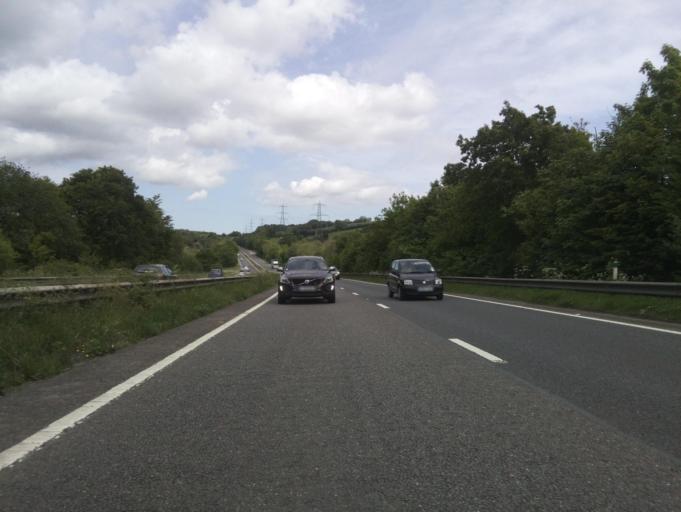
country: GB
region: England
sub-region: Devon
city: South Brent
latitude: 50.4216
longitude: -3.8183
